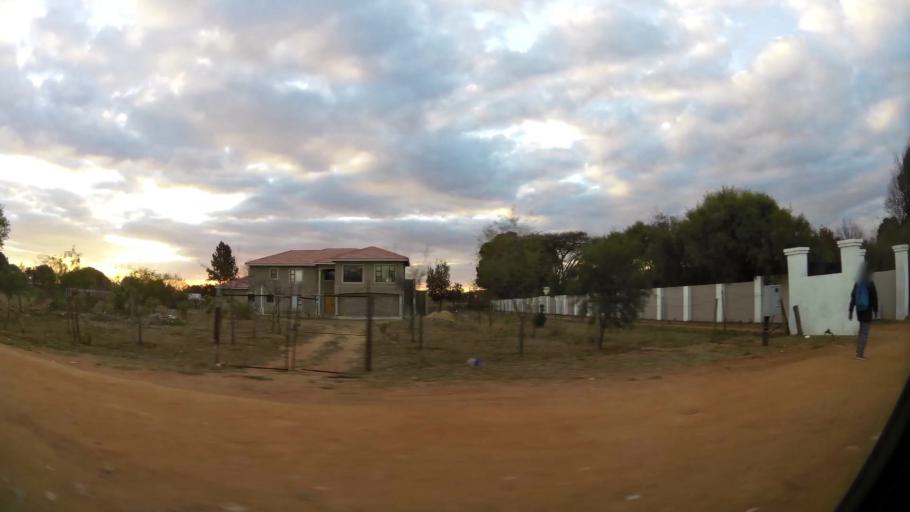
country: ZA
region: Gauteng
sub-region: City of Johannesburg Metropolitan Municipality
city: Midrand
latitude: -25.9864
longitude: 28.1565
